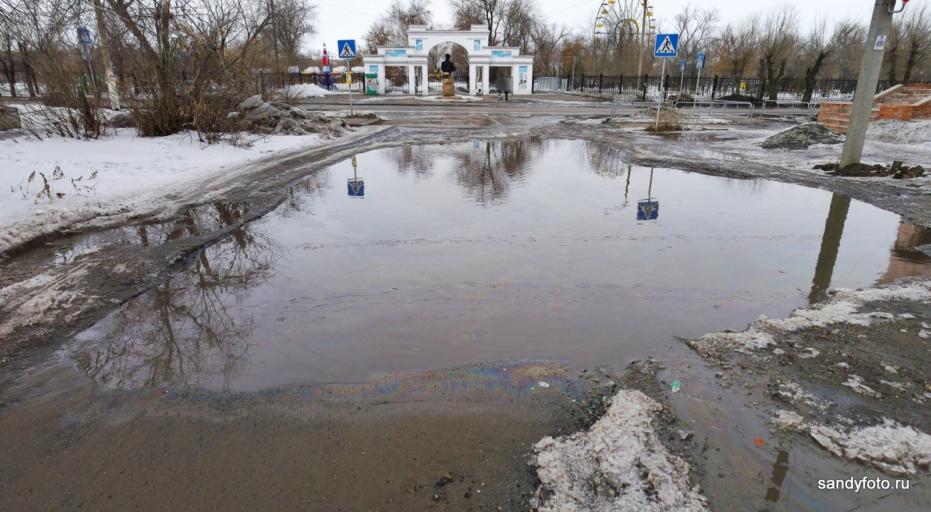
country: RU
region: Chelyabinsk
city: Troitsk
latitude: 54.0834
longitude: 61.5530
